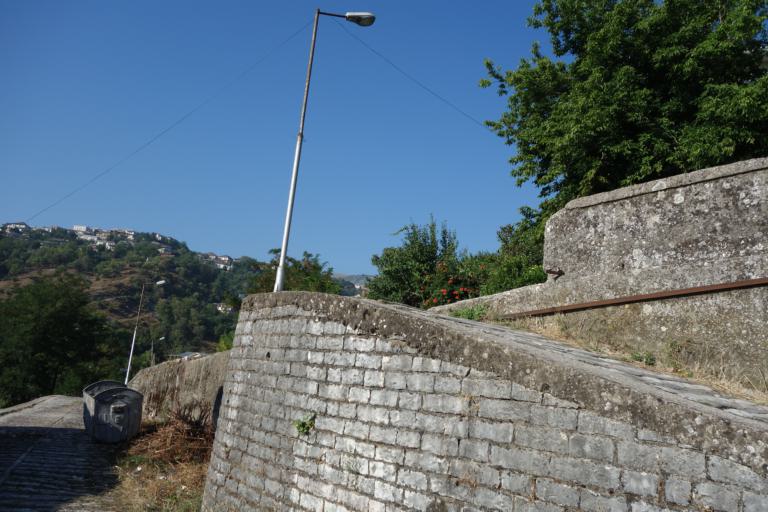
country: AL
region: Gjirokaster
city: Gjirokaster
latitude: 40.0774
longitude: 20.1462
